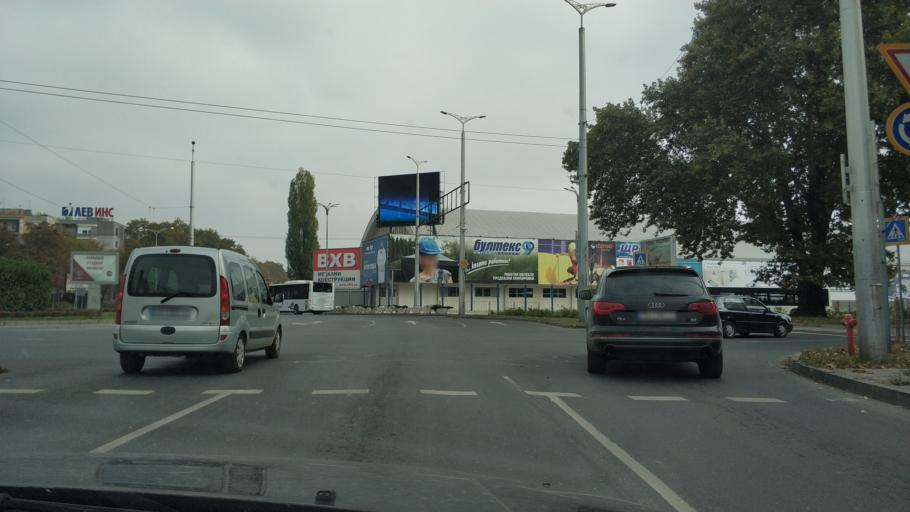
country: BG
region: Plovdiv
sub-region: Obshtina Plovdiv
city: Plovdiv
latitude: 42.1590
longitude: 24.7483
